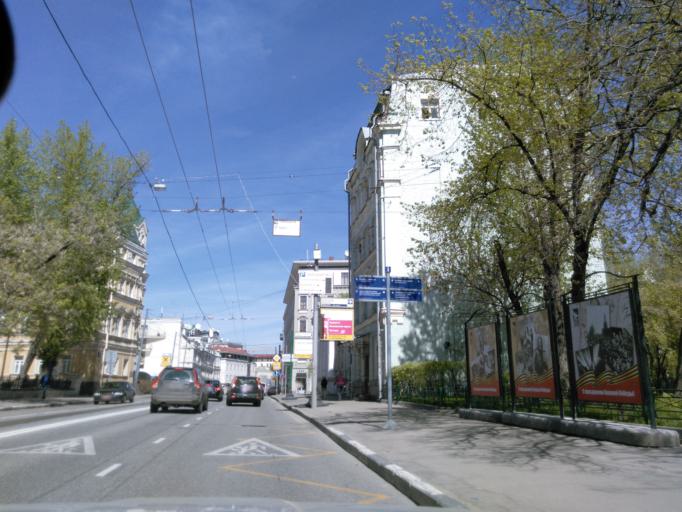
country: RU
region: Moscow
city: Moscow
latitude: 55.7383
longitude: 37.5956
